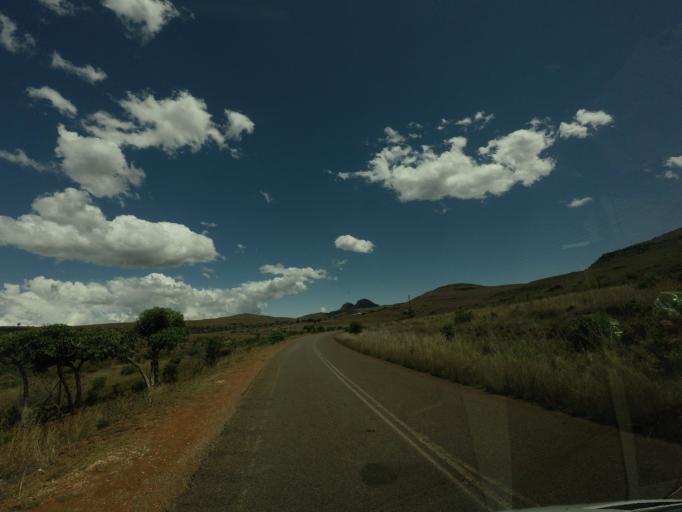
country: ZA
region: Limpopo
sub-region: Mopani District Municipality
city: Hoedspruit
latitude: -24.6004
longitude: 30.7891
